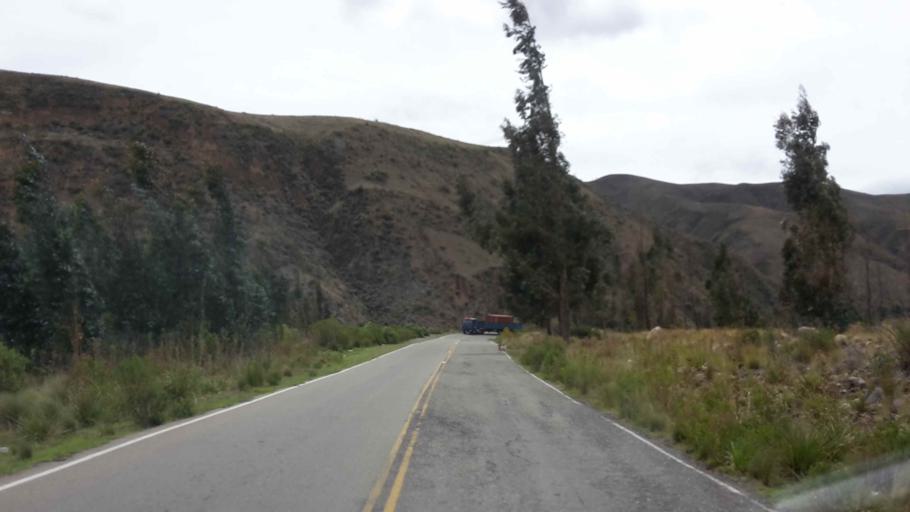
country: BO
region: Cochabamba
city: Colomi
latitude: -17.4137
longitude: -65.7719
